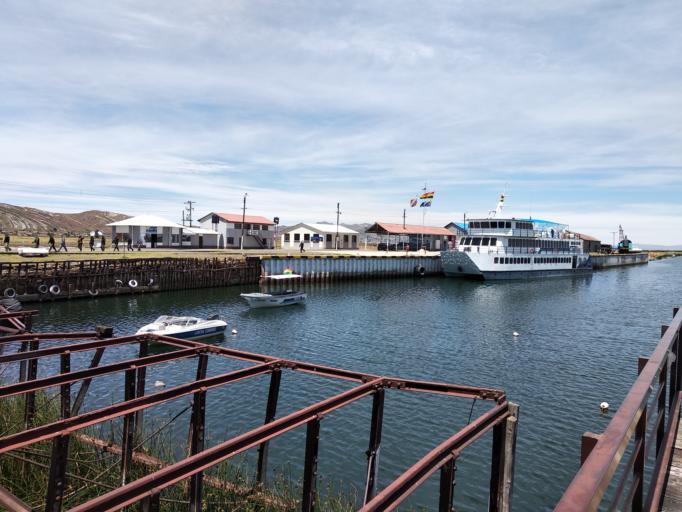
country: BO
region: La Paz
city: Tiahuanaco
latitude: -16.5908
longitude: -68.8547
